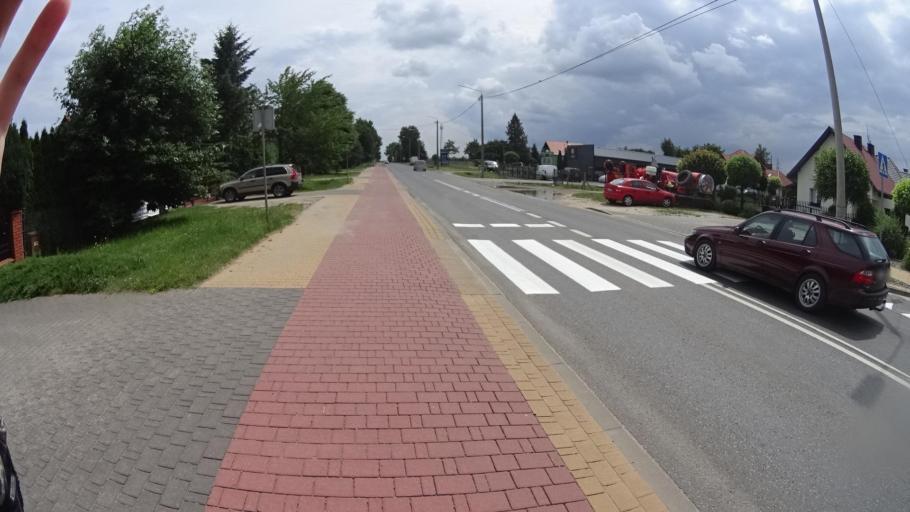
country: PL
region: Masovian Voivodeship
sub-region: Powiat grojecki
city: Grojec
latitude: 51.8527
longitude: 20.8715
